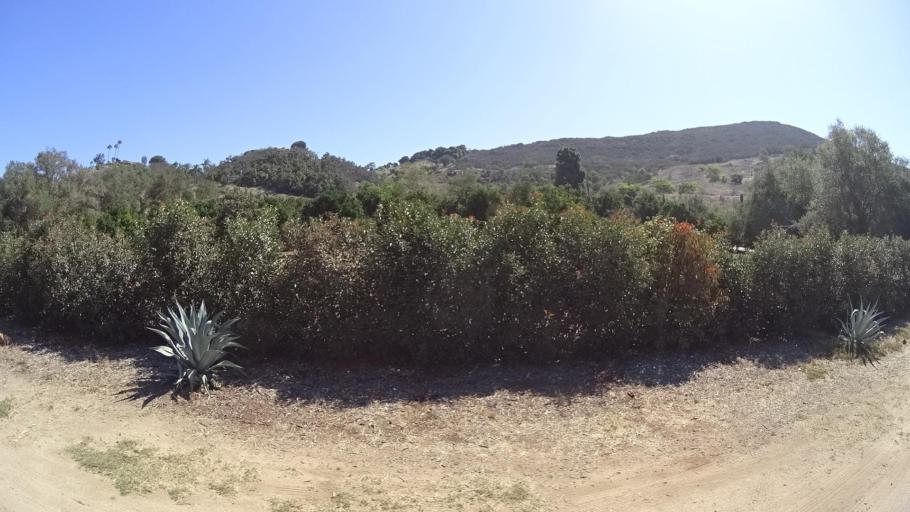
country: US
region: California
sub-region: San Diego County
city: Rainbow
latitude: 33.4173
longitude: -117.1757
